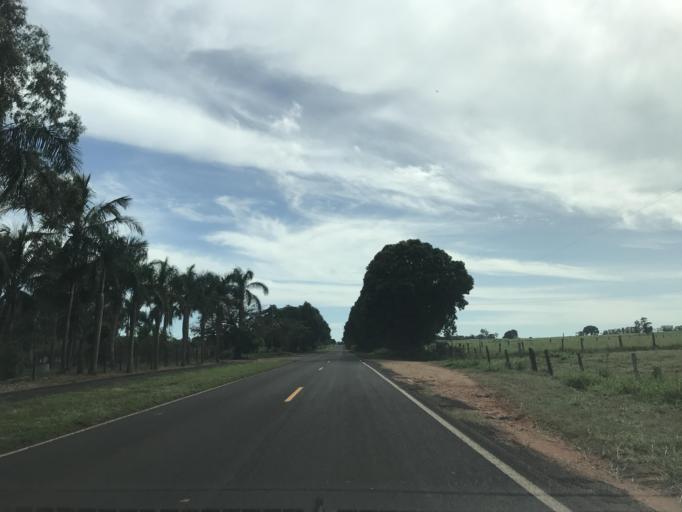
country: BR
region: Parana
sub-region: Terra Rica
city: Terra Rica
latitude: -22.7603
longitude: -52.6339
